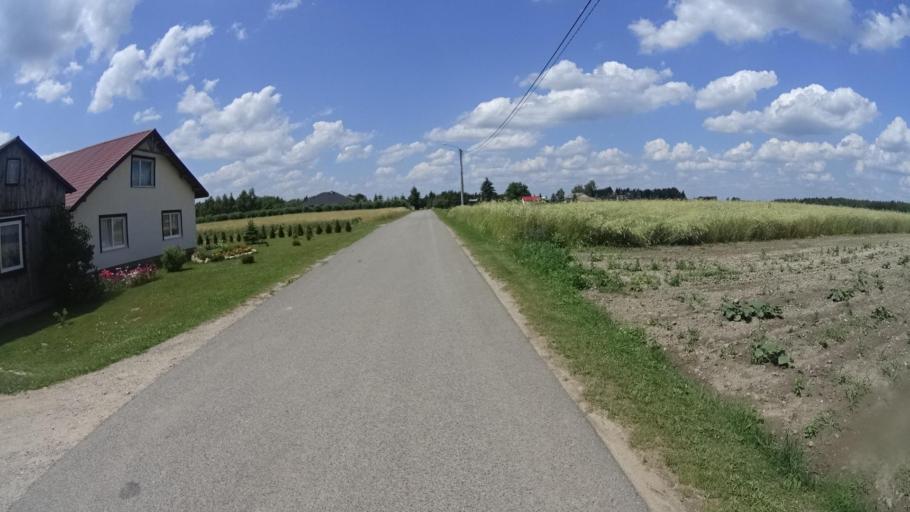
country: PL
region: Masovian Voivodeship
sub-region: Powiat bialobrzeski
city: Promna
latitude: 51.7098
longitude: 20.9140
